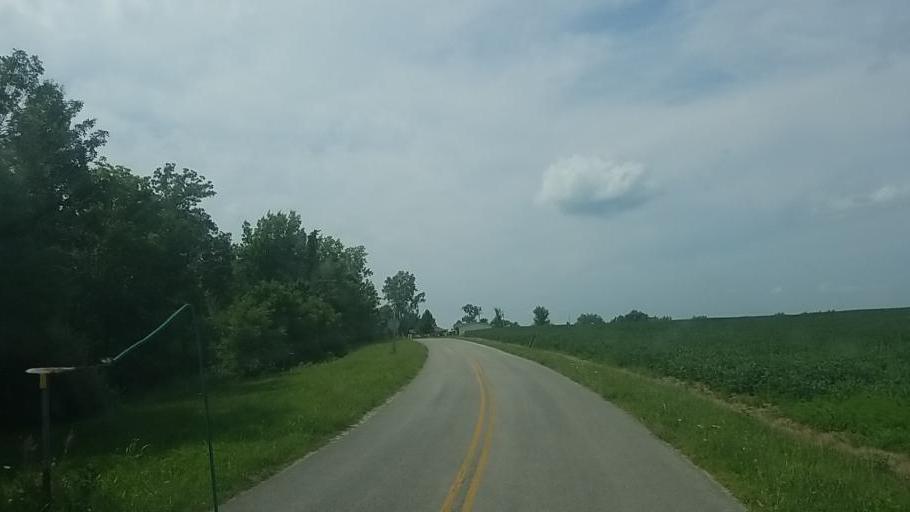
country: US
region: Ohio
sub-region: Hardin County
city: Forest
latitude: 40.8001
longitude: -83.5508
